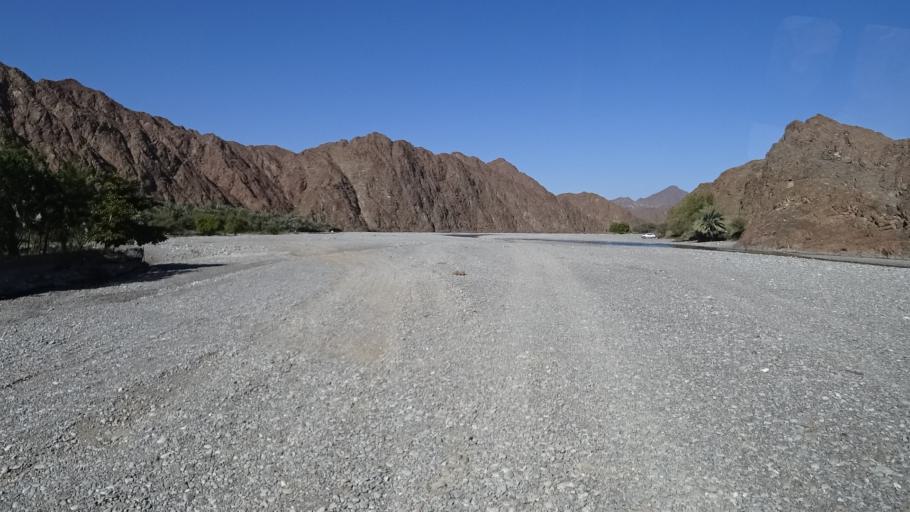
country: OM
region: Al Batinah
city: Bayt al `Awabi
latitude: 23.3950
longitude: 57.6629
